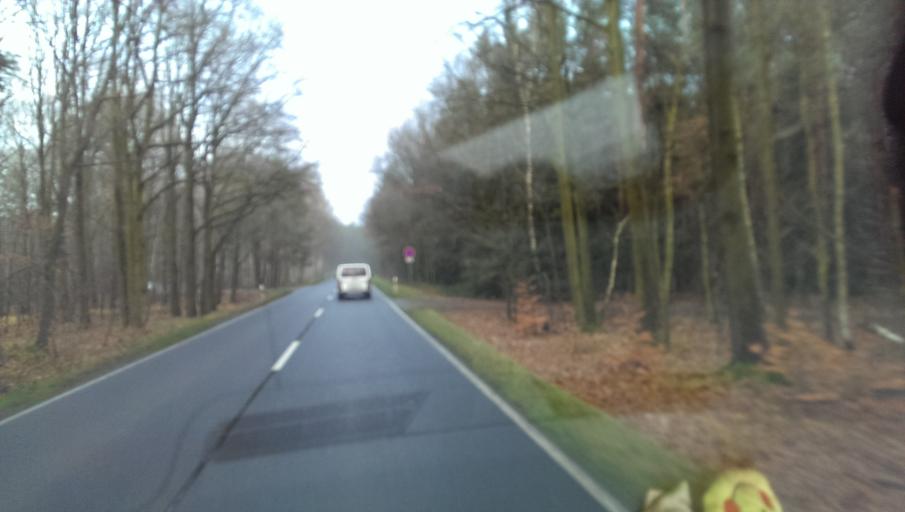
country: DE
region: Saxony
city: Weinbohla
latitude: 51.1830
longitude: 13.6141
